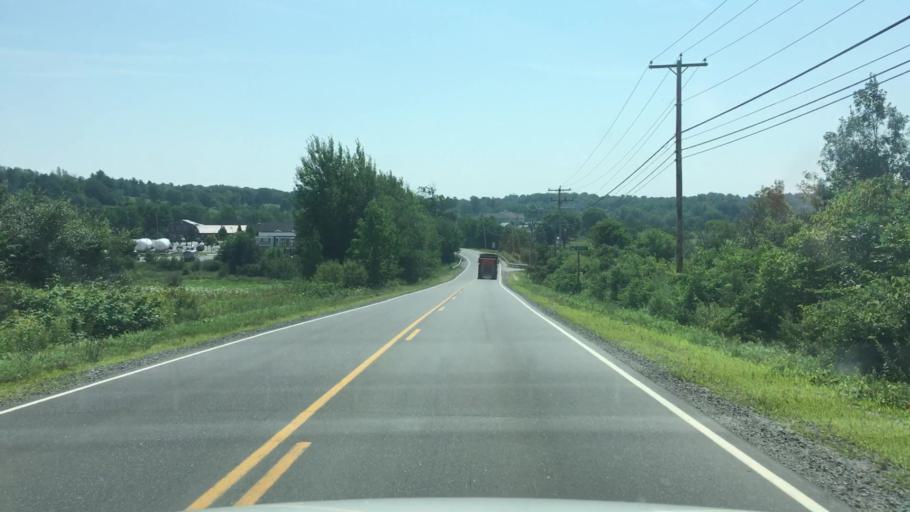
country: US
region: Maine
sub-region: Kennebec County
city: Hallowell
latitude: 44.3002
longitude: -69.8131
